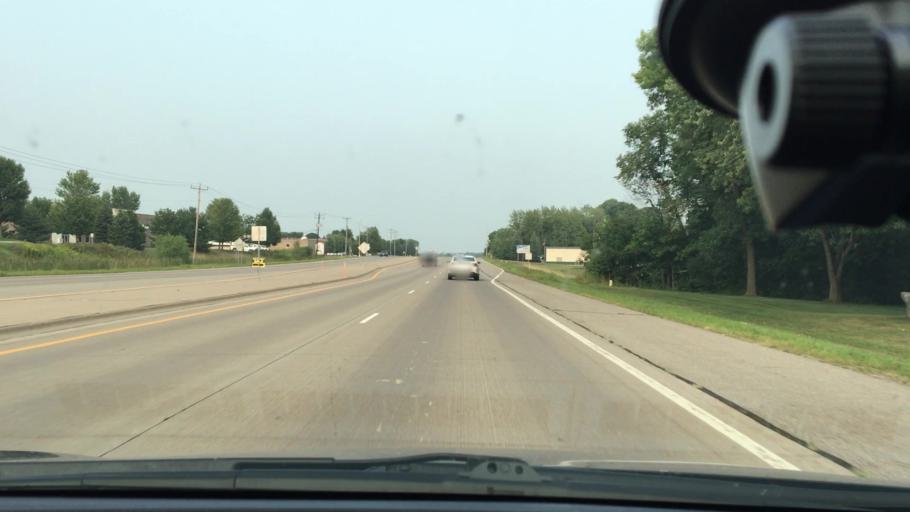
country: US
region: Minnesota
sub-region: Wright County
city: Saint Michael
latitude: 45.2107
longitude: -93.6427
